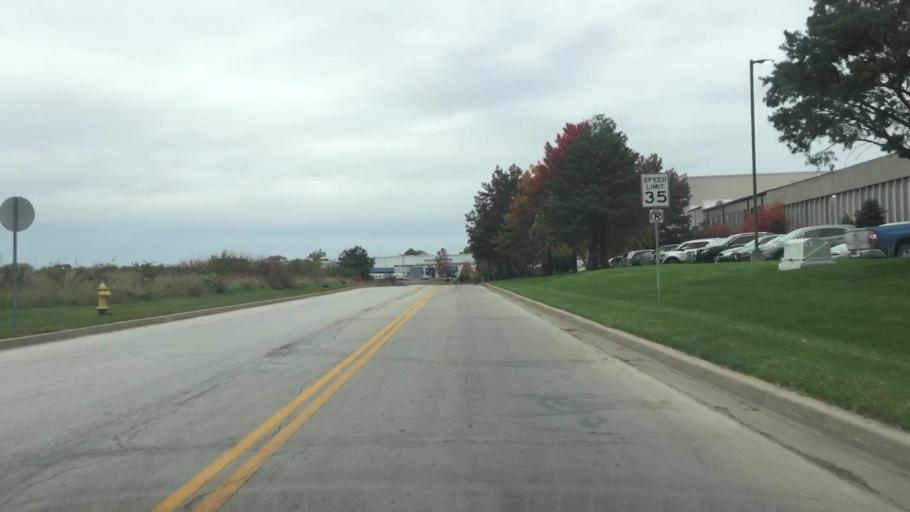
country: US
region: Missouri
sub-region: Jackson County
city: Lees Summit
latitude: 38.8862
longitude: -94.3634
